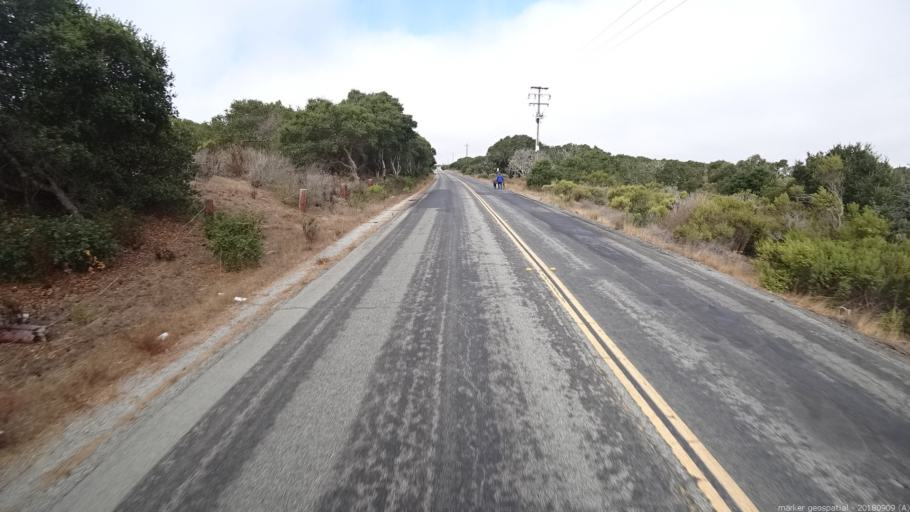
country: US
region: California
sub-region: Monterey County
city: Marina
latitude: 36.6555
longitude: -121.7469
